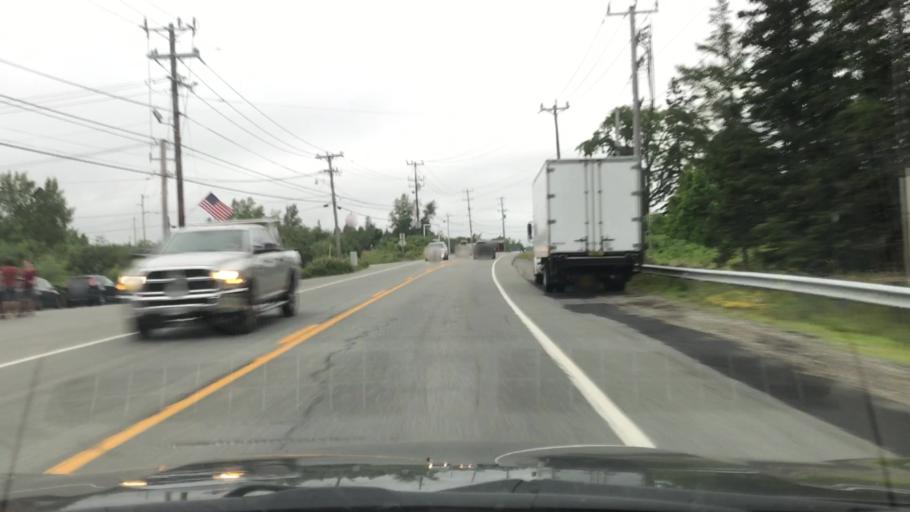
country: US
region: Maine
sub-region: Hancock County
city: Trenton
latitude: 44.4324
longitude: -68.3684
